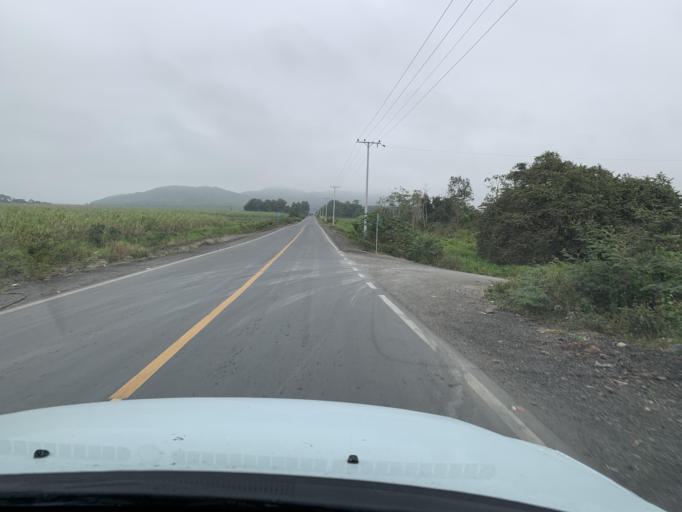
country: EC
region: Guayas
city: Coronel Marcelino Mariduena
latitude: -2.3355
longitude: -79.5293
